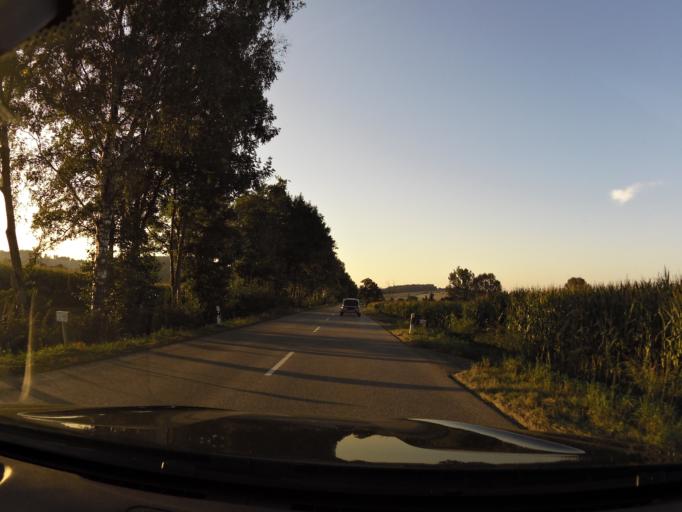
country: DE
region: Bavaria
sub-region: Lower Bavaria
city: Postau
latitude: 48.6364
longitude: 12.3204
